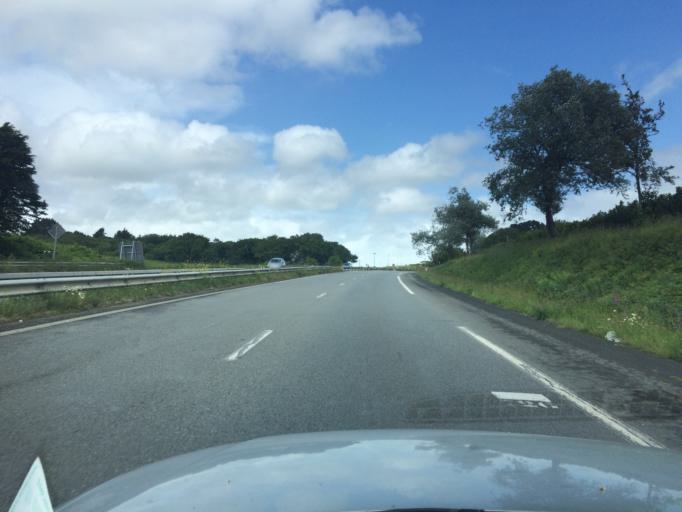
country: FR
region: Brittany
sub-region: Departement du Finistere
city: Gouesnou
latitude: 48.4308
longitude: -4.4725
